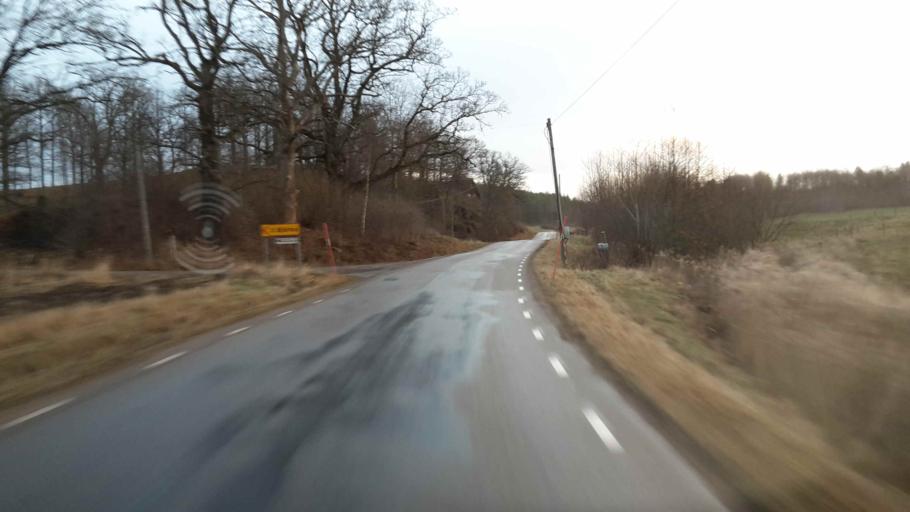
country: SE
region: Kalmar
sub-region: Vasterviks Kommun
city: Overum
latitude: 58.1538
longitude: 16.3031
